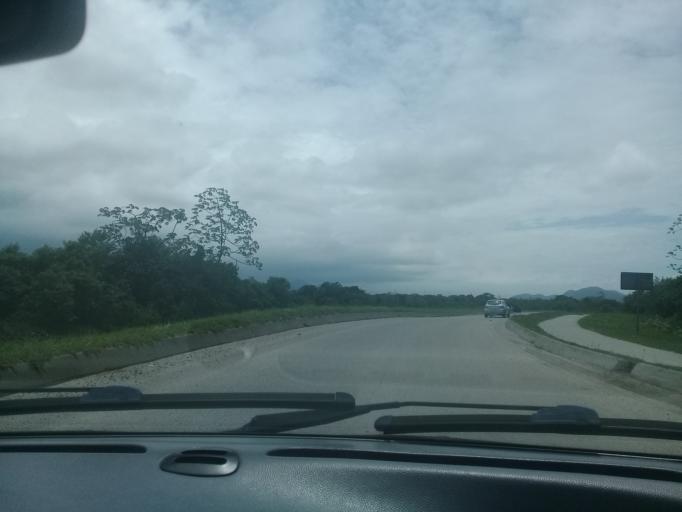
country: BR
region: Sao Paulo
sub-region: Guaruja
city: Guaruja
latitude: -23.9708
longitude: -46.2691
